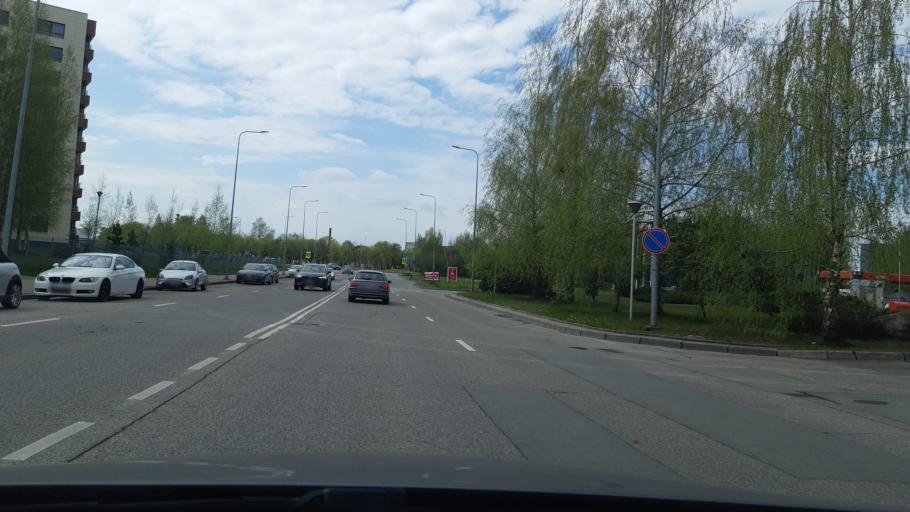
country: LT
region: Kauno apskritis
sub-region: Kaunas
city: Silainiai
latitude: 54.9177
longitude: 23.8644
